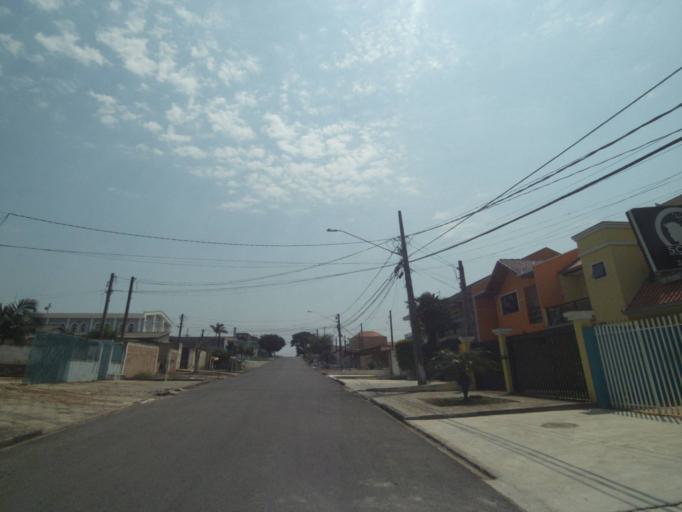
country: BR
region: Parana
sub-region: Sao Jose Dos Pinhais
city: Sao Jose dos Pinhais
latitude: -25.5370
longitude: -49.2449
